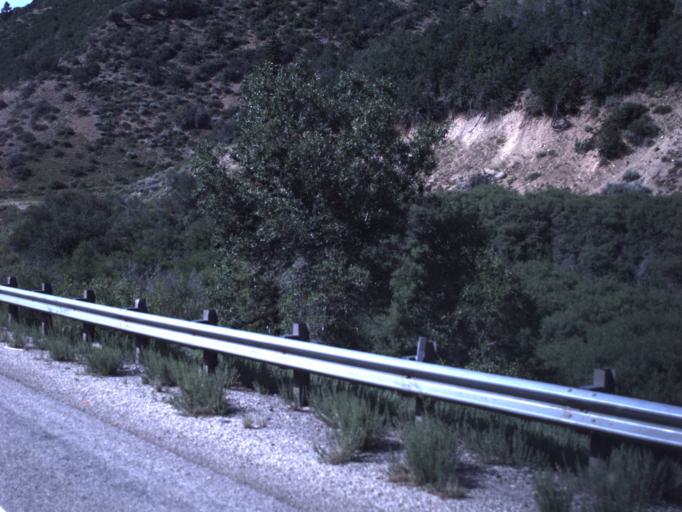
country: US
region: Utah
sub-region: Wasatch County
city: Heber
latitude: 40.3479
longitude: -111.2694
